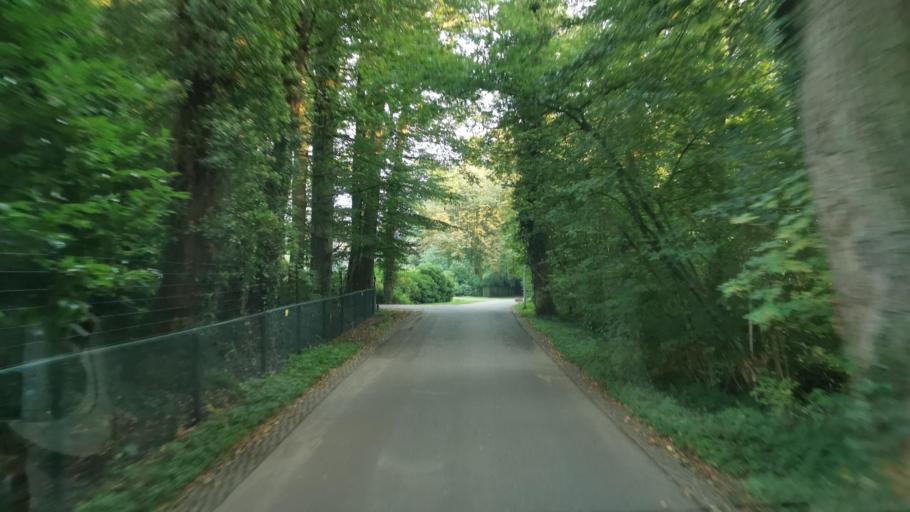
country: NL
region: Overijssel
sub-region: Gemeente Oldenzaal
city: Oldenzaal
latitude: 52.3144
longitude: 6.9464
